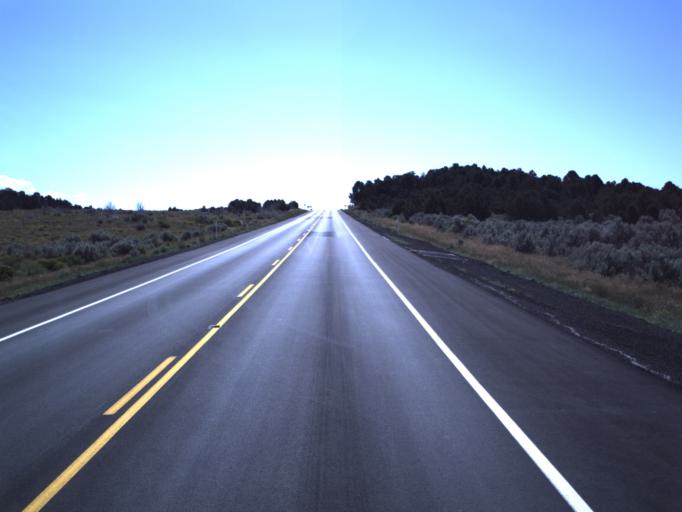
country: US
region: Utah
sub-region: Utah County
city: Genola
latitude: 39.9609
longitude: -112.2471
